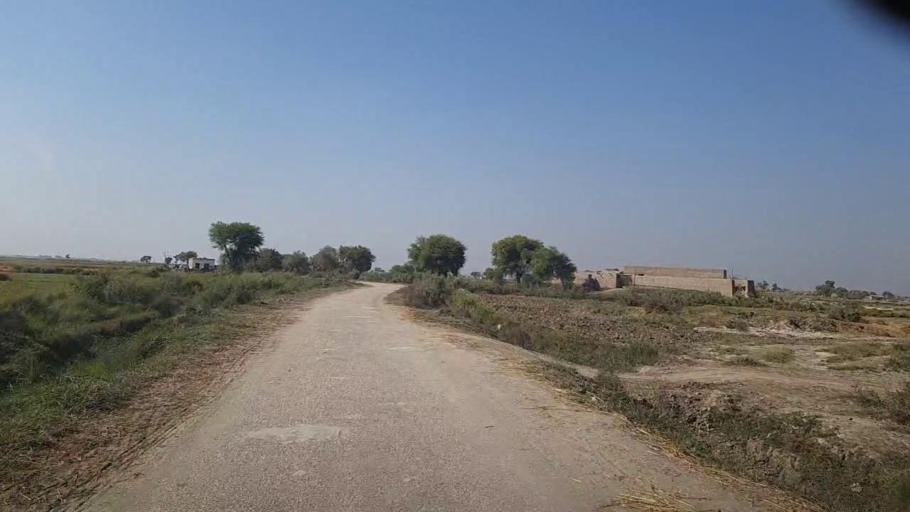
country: PK
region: Sindh
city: Tangwani
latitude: 28.2493
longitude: 68.9431
